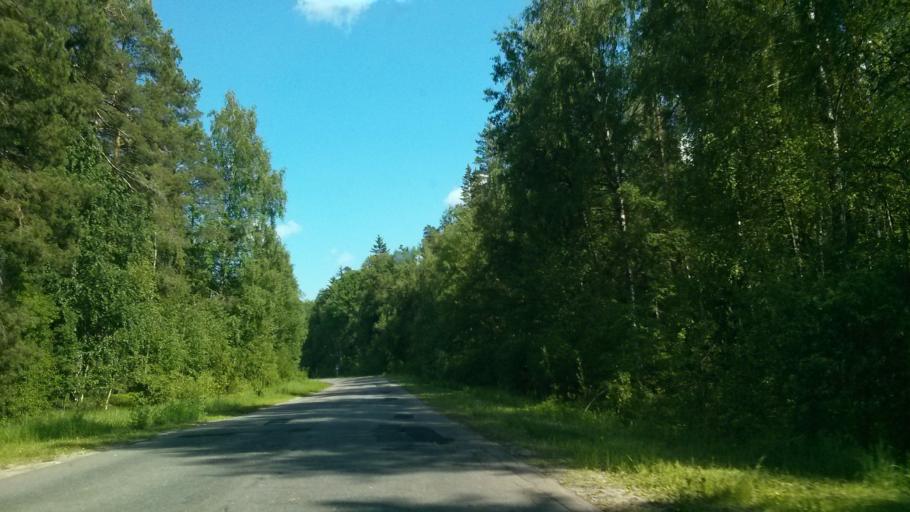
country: RU
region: Vladimir
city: Melenki
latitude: 55.3325
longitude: 41.6845
